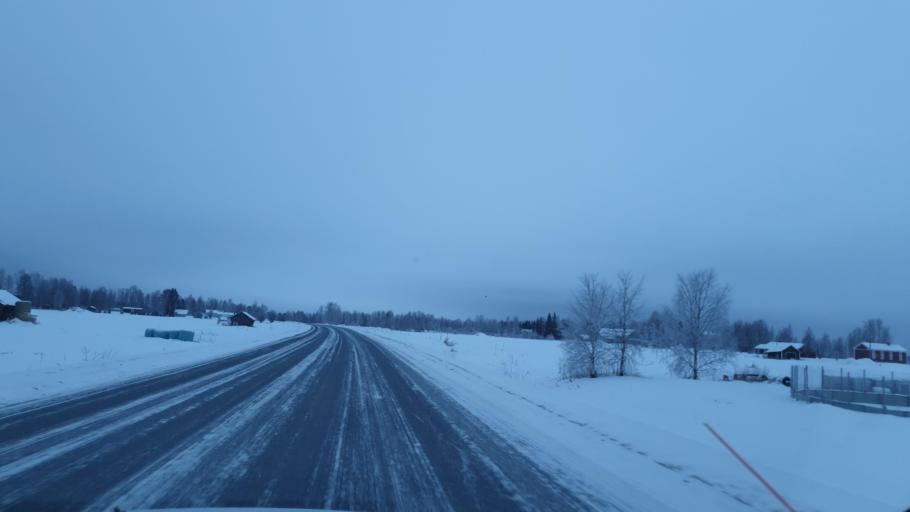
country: SE
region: Norrbotten
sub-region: Overtornea Kommun
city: OEvertornea
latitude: 66.4242
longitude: 23.6634
